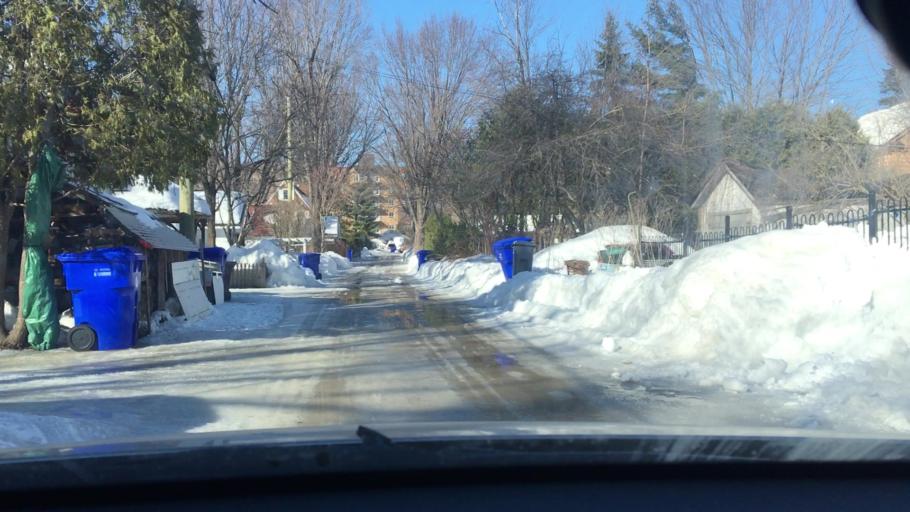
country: CA
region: Quebec
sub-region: Outaouais
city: Gatineau
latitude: 45.4803
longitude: -75.6485
